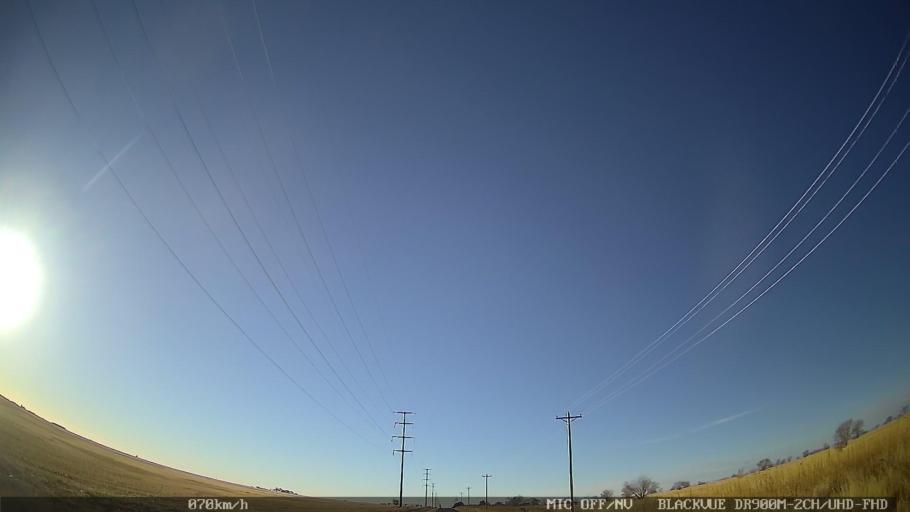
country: US
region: New Mexico
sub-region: Curry County
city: Clovis
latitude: 34.4299
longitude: -103.2493
